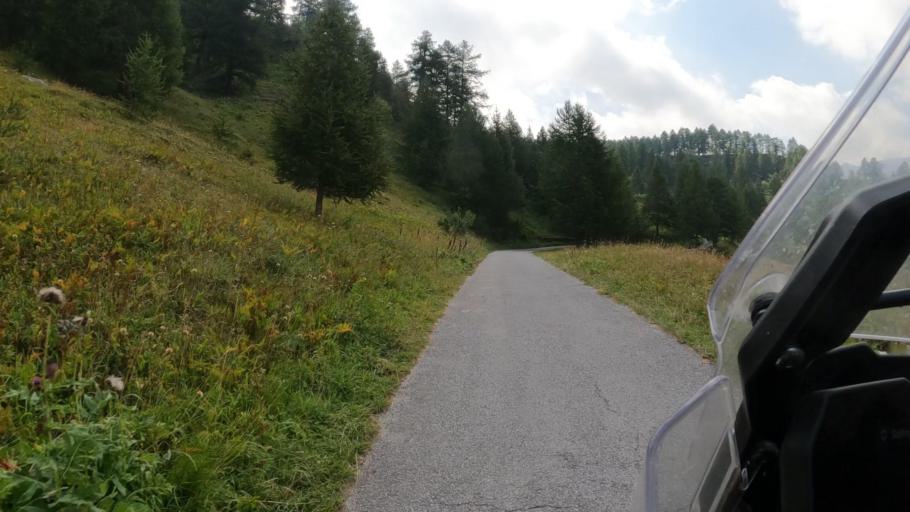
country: IT
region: Piedmont
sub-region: Provincia di Cuneo
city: Marmora
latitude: 44.4188
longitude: 7.1058
